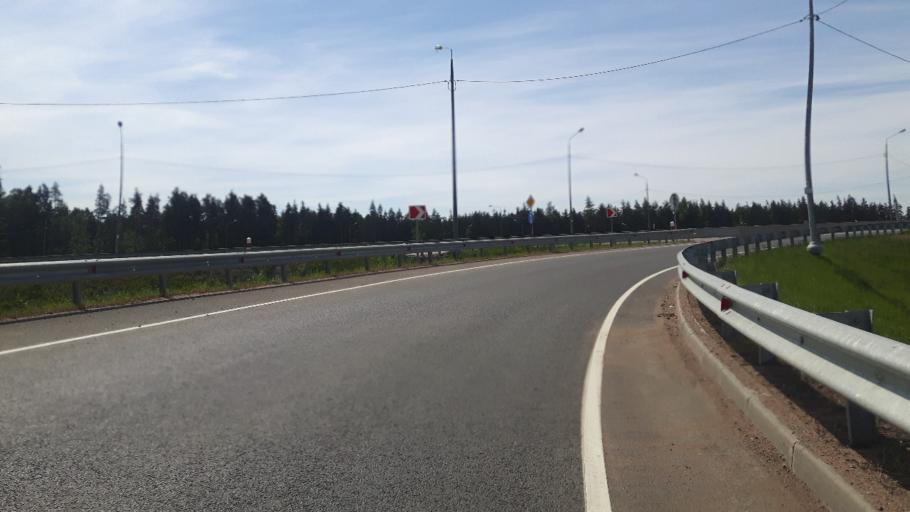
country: RU
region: Leningrad
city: Vistino
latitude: 59.6628
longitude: 28.4406
